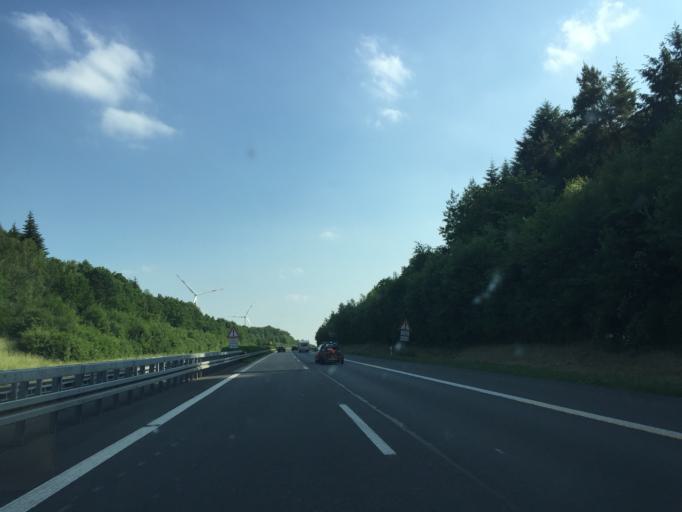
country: DE
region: Baden-Wuerttemberg
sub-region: Regierungsbezirk Stuttgart
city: Buch am Ahorn
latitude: 49.5203
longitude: 9.5706
